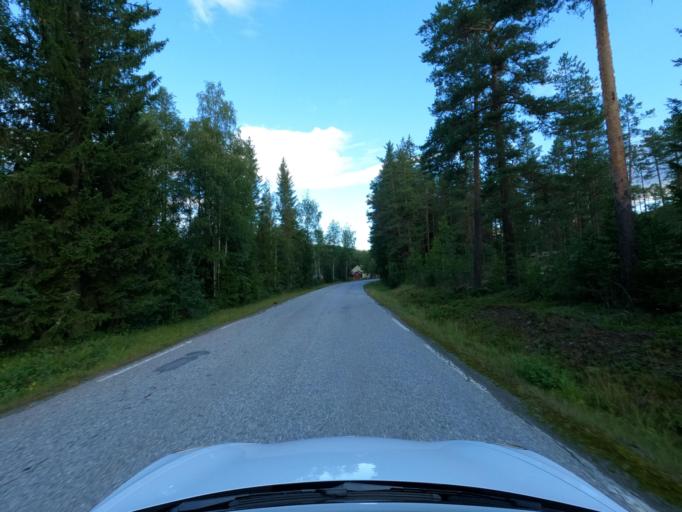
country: NO
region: Telemark
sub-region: Hjartdal
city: Sauland
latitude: 59.8190
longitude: 9.0674
